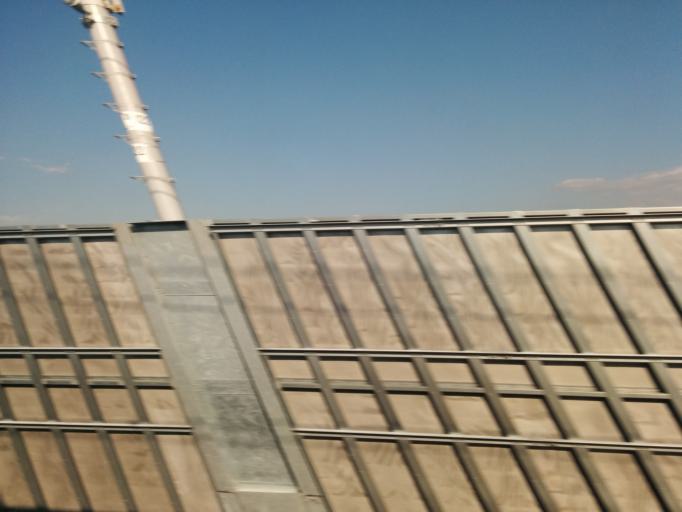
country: JP
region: Aichi
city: Okazaki
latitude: 34.9004
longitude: 137.1237
